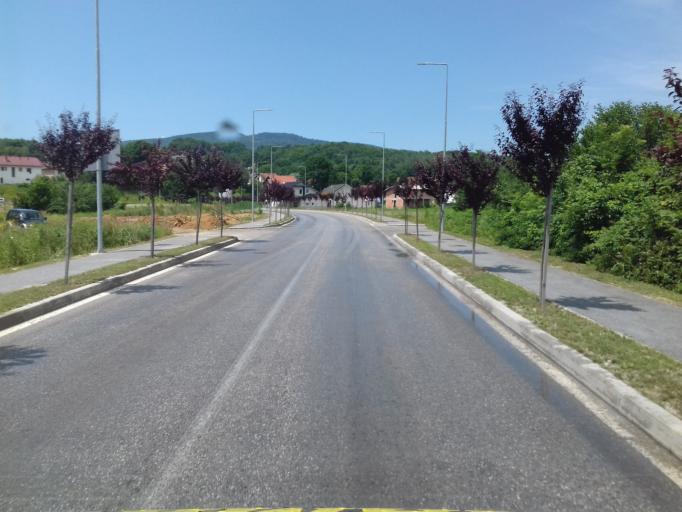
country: BA
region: Federation of Bosnia and Herzegovina
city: Kiseljak
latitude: 43.9482
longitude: 18.0767
